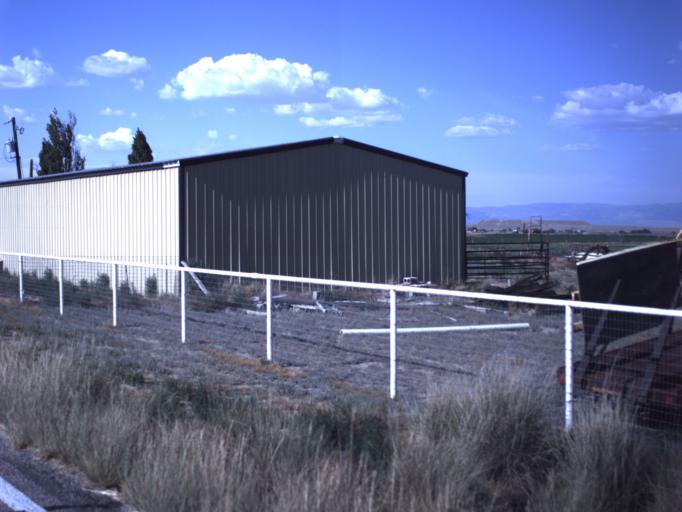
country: US
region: Utah
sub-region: Emery County
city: Huntington
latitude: 39.4048
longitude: -110.8525
